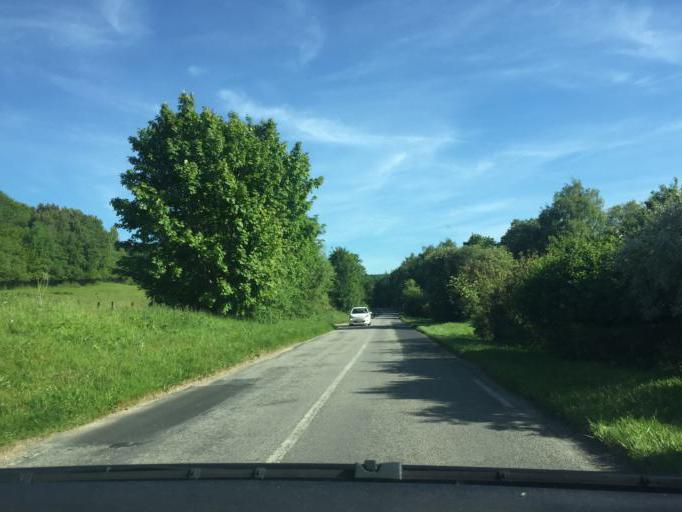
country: FR
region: Ile-de-France
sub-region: Departement de l'Essonne
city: Villiers-le-Bacle
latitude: 48.7102
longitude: 2.1202
